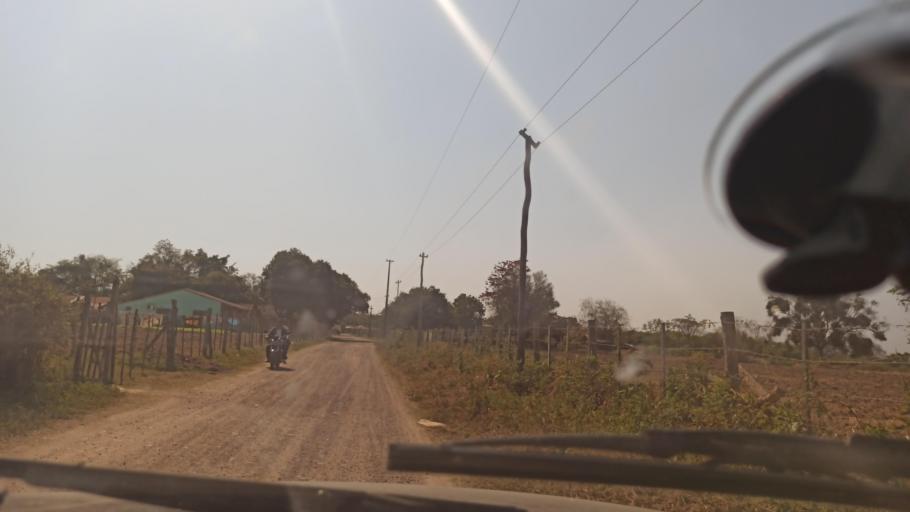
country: AR
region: Formosa
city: Clorinda
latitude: -25.3110
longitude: -57.6976
